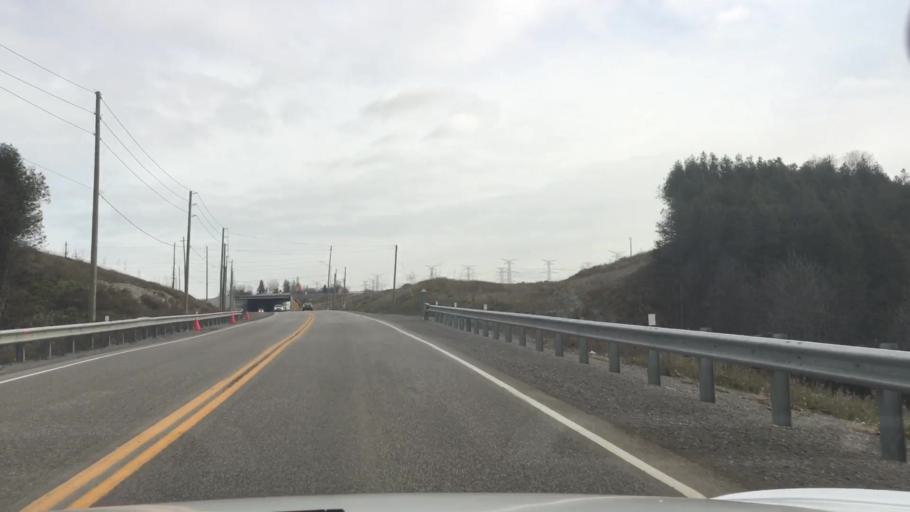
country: CA
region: Ontario
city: Oshawa
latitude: 43.9613
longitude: -78.9269
